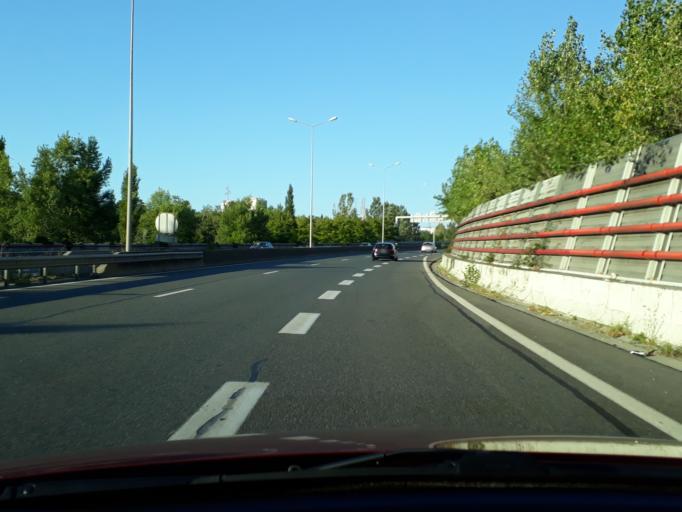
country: FR
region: Rhone-Alpes
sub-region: Departement du Rhone
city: Feyzin
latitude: 45.6823
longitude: 4.8513
